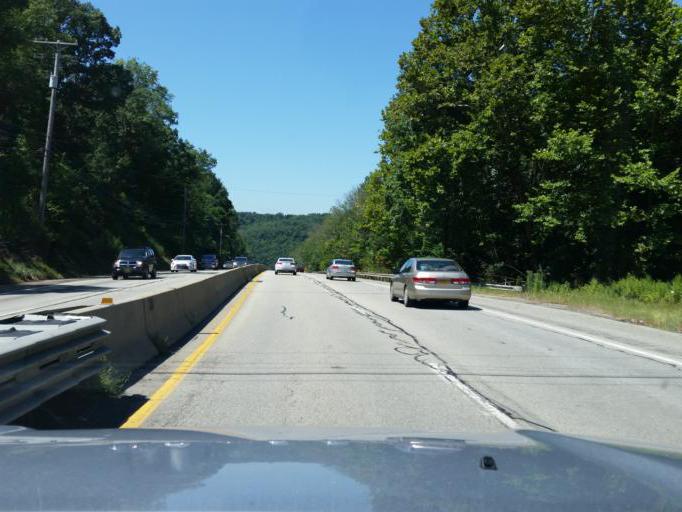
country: US
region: Pennsylvania
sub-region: Westmoreland County
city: Murrysville
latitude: 40.4303
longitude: -79.7135
